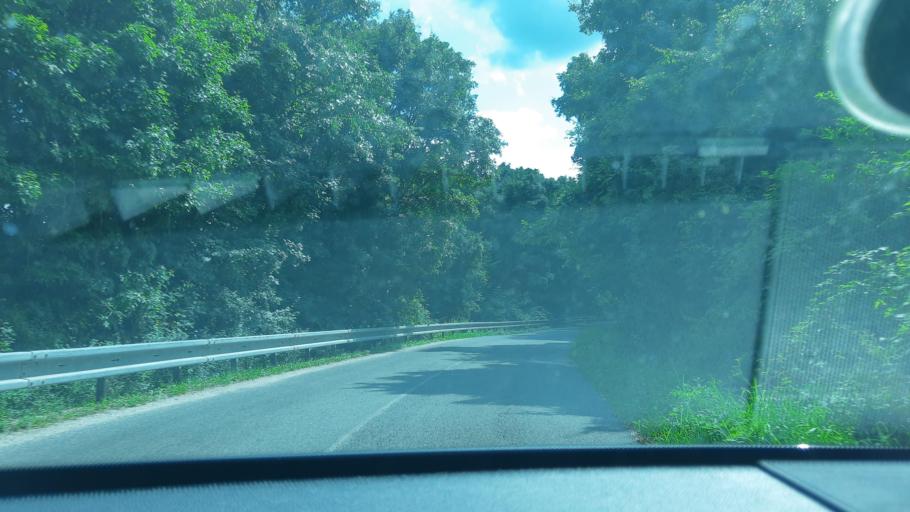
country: SK
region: Trnavsky
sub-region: Okres Trnava
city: Piestany
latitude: 48.6577
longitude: 17.9575
